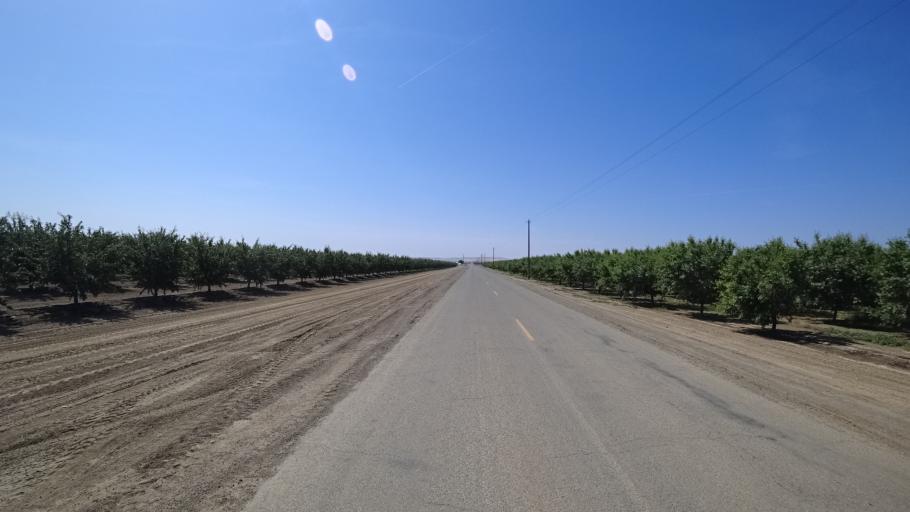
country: US
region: California
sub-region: Kings County
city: Kettleman City
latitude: 36.0833
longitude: -120.0036
